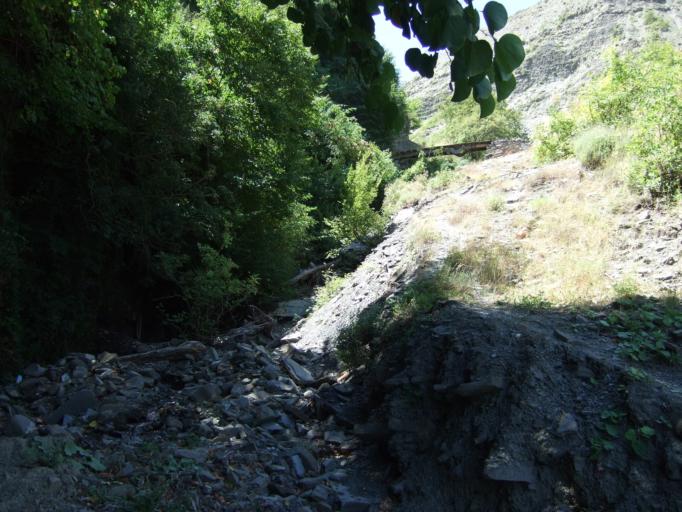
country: AL
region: Gjirokaster
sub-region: Rrethi i Permetit
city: Frasher
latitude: 40.2946
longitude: 20.4705
